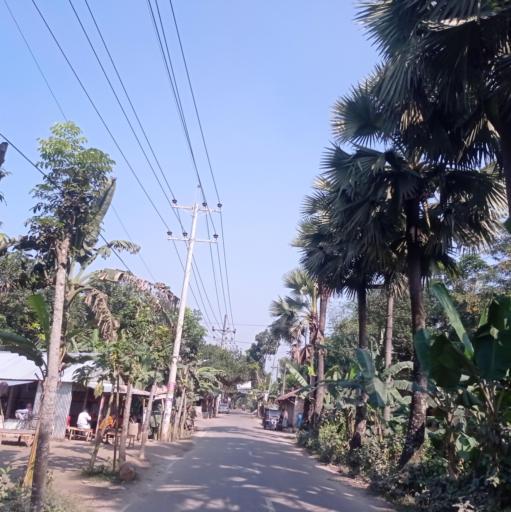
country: BD
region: Dhaka
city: Narsingdi
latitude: 24.0251
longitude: 90.6698
